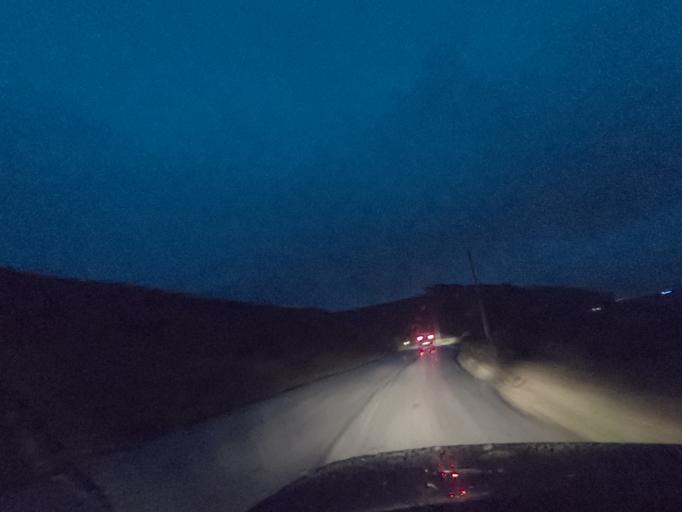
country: PT
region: Vila Real
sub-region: Sabrosa
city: Vilela
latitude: 41.2330
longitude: -7.5709
